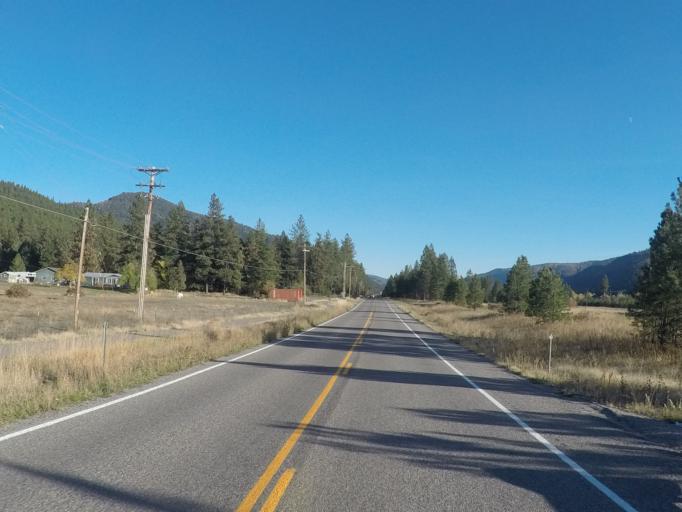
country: US
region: Montana
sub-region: Missoula County
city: Bonner-West Riverside
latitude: 46.8452
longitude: -113.8431
